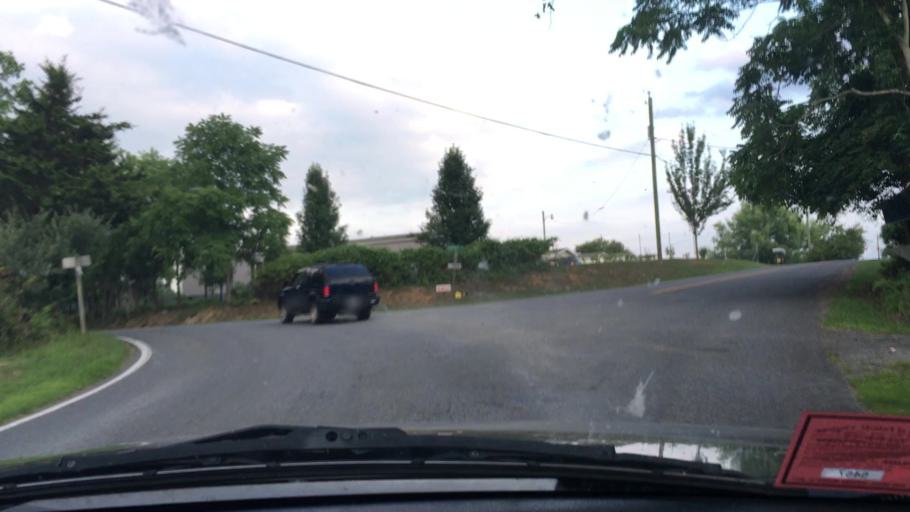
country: US
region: Virginia
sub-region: Pulaski County
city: Dublin
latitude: 37.0539
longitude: -80.6964
